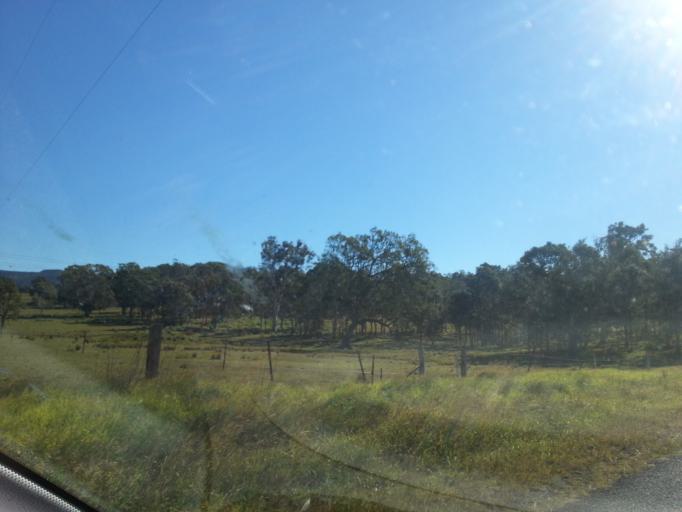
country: AU
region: New South Wales
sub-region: Wollongong
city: Dapto
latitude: -34.5221
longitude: 150.7790
